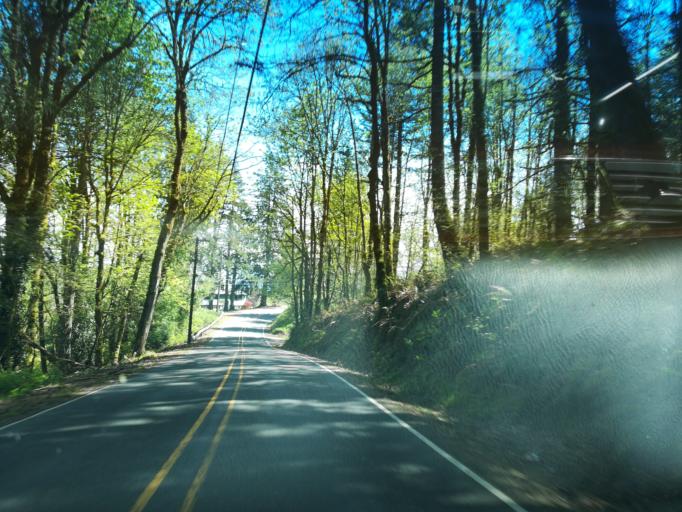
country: US
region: Oregon
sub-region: Clackamas County
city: Damascus
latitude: 45.4534
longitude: -122.4355
